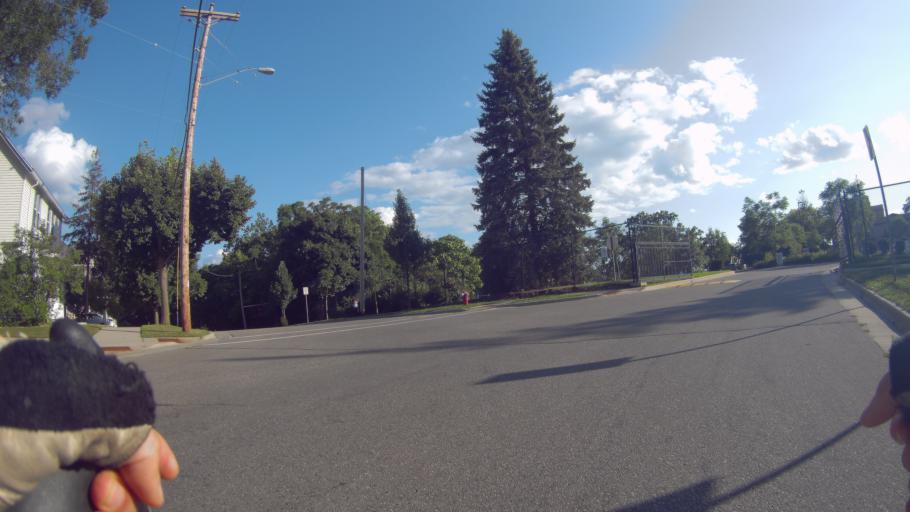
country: US
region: Wisconsin
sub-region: Dane County
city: Madison
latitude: 43.0611
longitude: -89.4195
